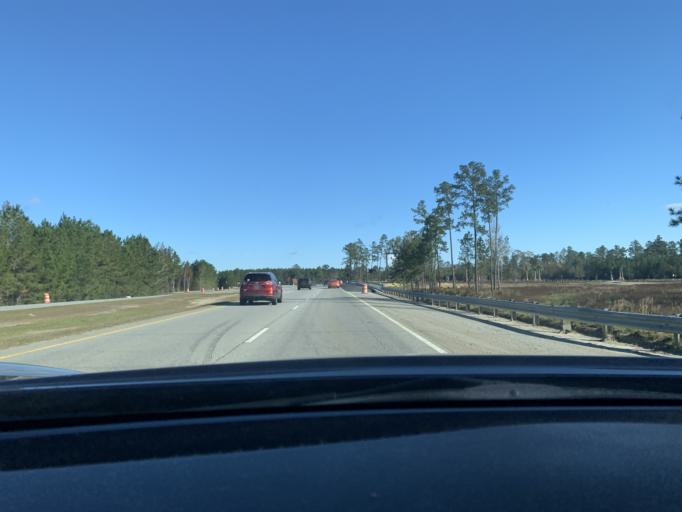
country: US
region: Georgia
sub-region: Chatham County
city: Pooler
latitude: 32.1030
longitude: -81.2680
